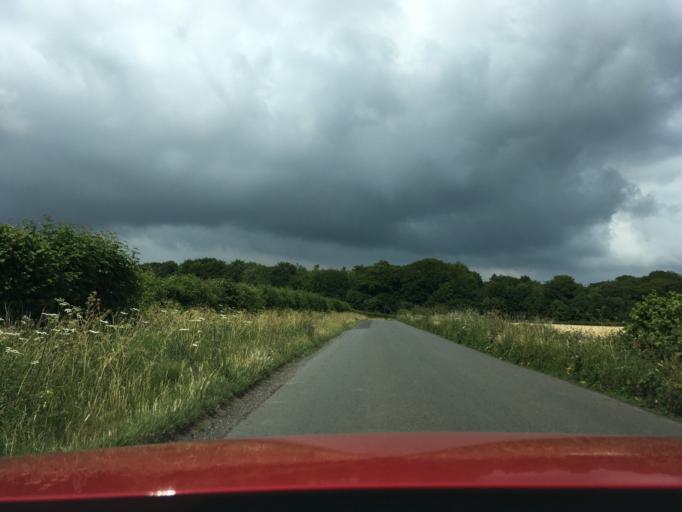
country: GB
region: England
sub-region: Gloucestershire
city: Coates
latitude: 51.7169
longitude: -2.0885
